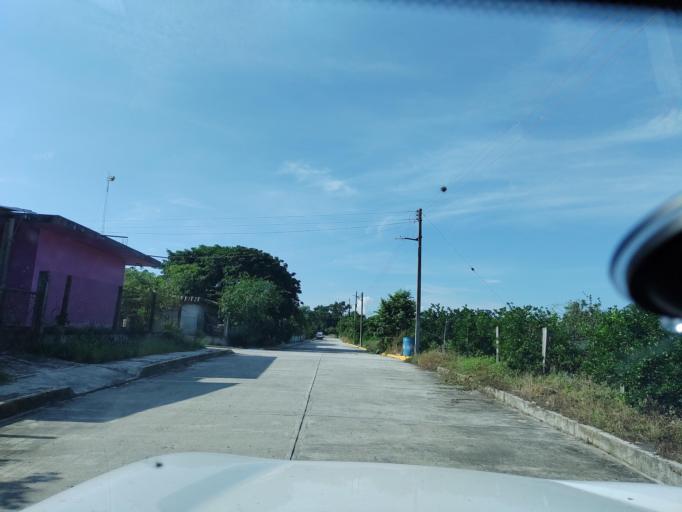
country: MX
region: Veracruz
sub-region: Martinez de la Torre
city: El Progreso
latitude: 20.1136
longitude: -96.9879
